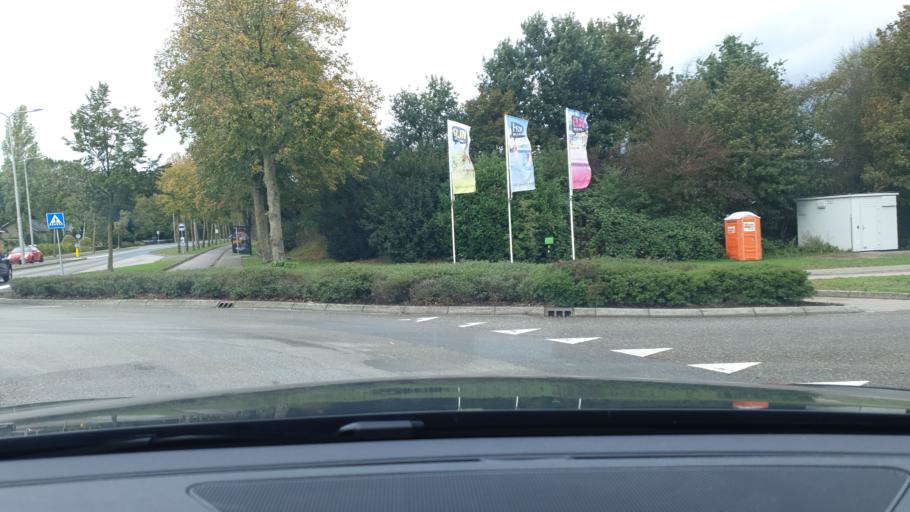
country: NL
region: Limburg
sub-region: Gemeente Venlo
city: Venlo
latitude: 51.4080
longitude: 6.1670
